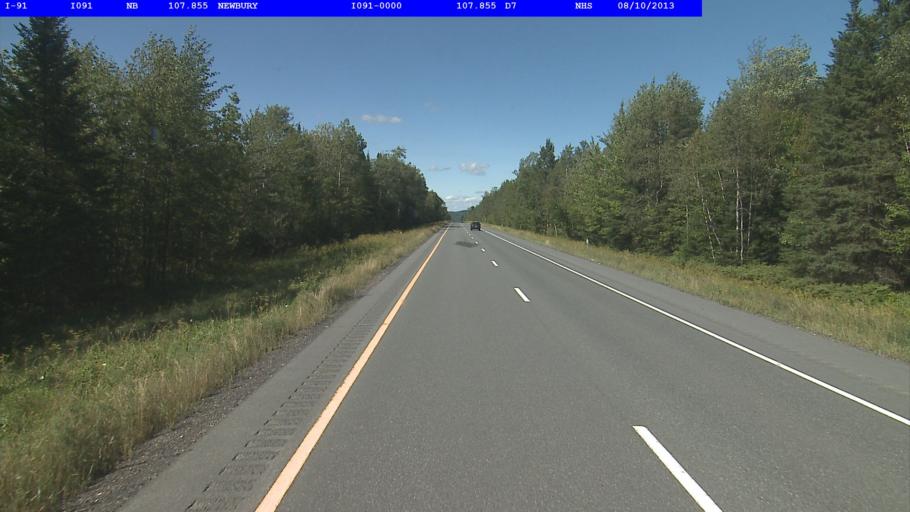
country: US
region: New Hampshire
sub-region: Grafton County
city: Woodsville
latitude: 44.1263
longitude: -72.1038
